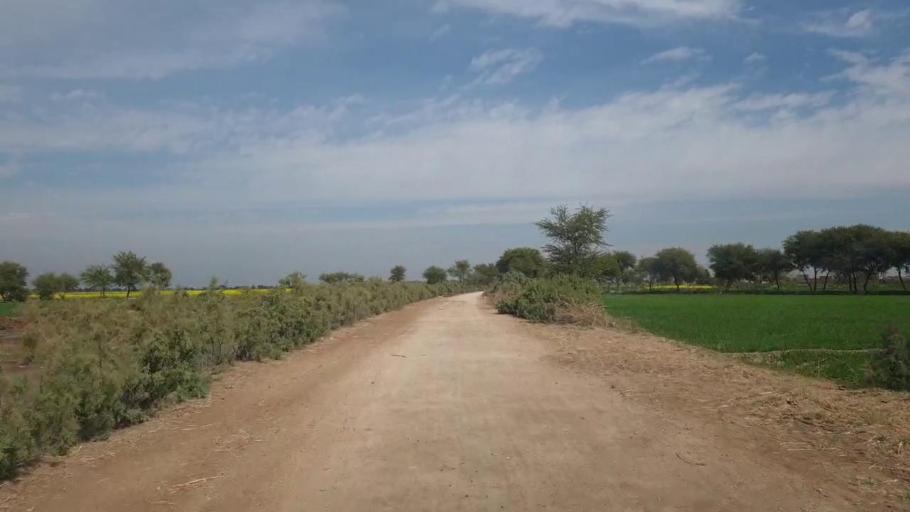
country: PK
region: Sindh
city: Sanghar
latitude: 26.0490
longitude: 68.9049
